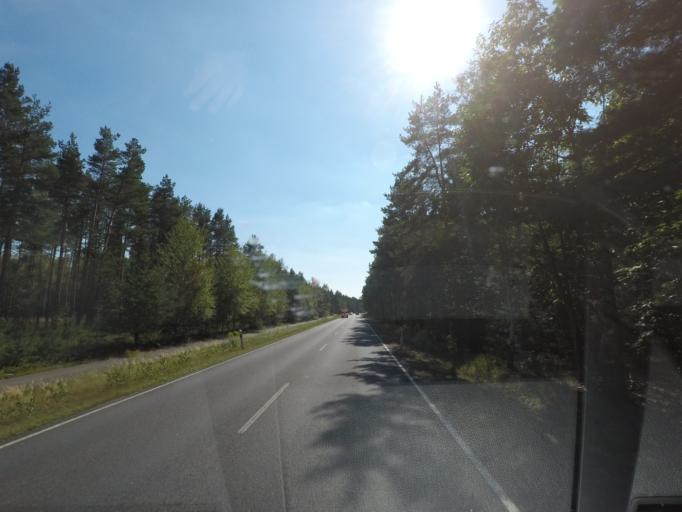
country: DE
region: Brandenburg
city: Schipkau
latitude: 51.4988
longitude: 13.8966
